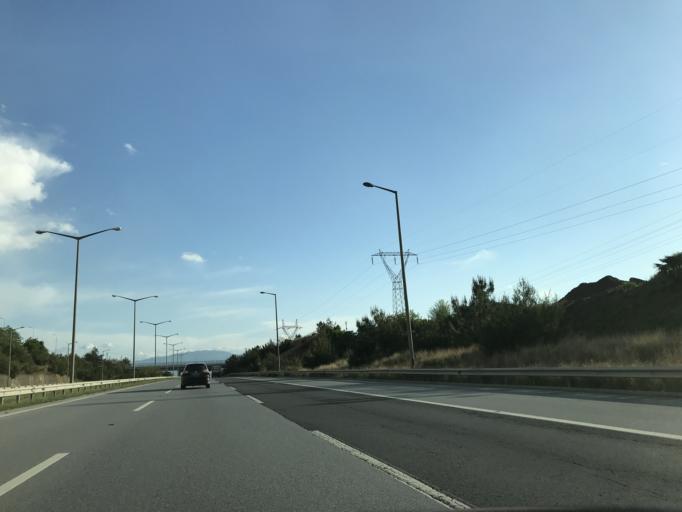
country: TR
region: Hatay
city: Yakacik
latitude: 36.7119
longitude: 36.2209
